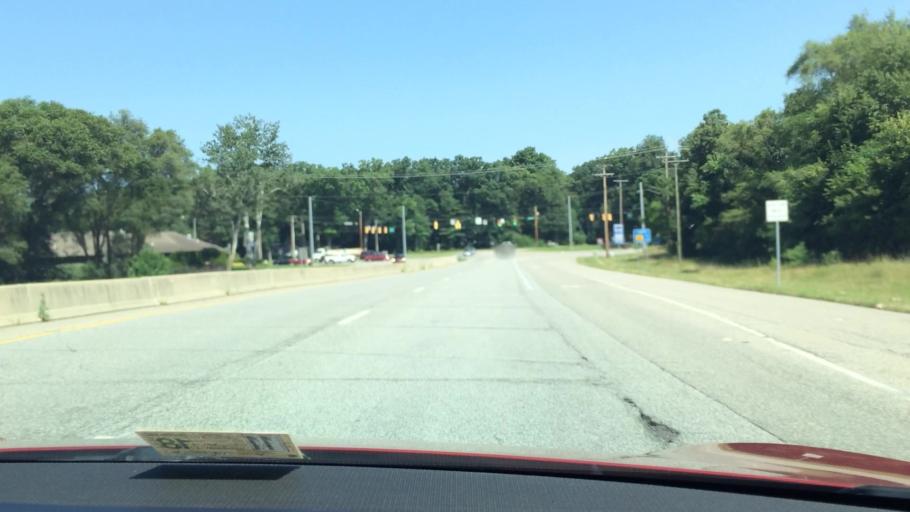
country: US
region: Indiana
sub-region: Saint Joseph County
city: Granger
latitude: 41.7355
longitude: -86.1509
